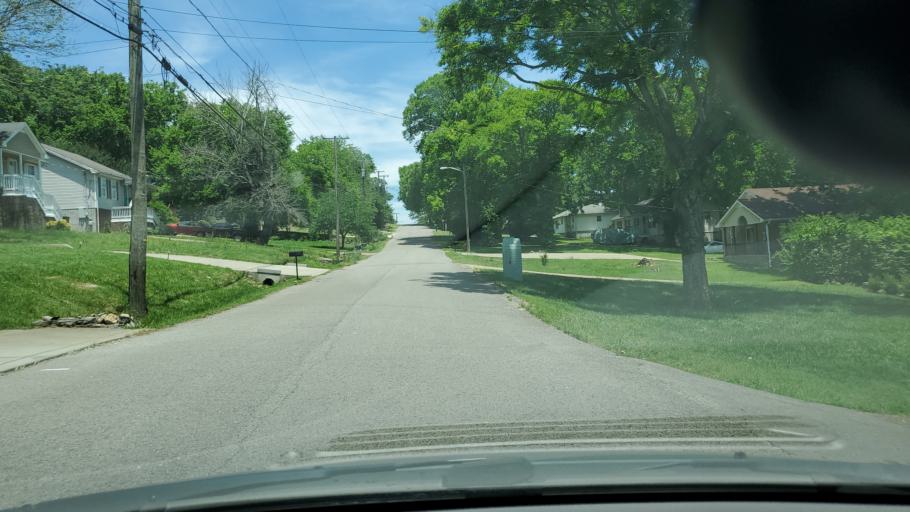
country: US
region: Tennessee
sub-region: Davidson County
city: Nashville
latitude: 36.2200
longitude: -86.7406
